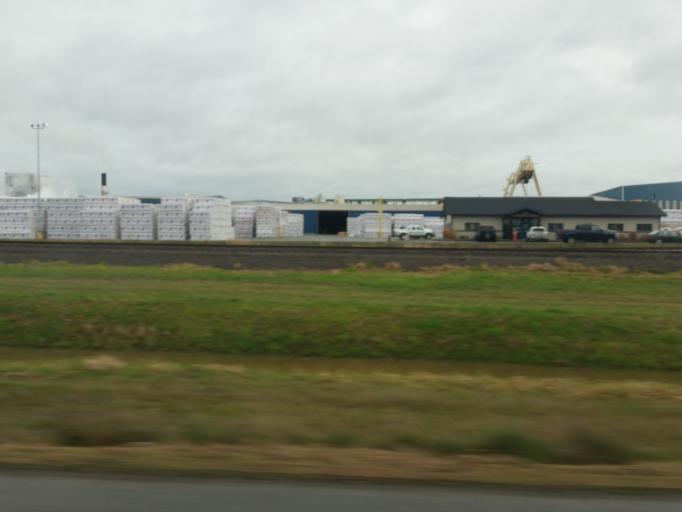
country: US
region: Washington
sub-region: Skagit County
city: Mount Vernon
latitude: 48.4463
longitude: -122.4345
